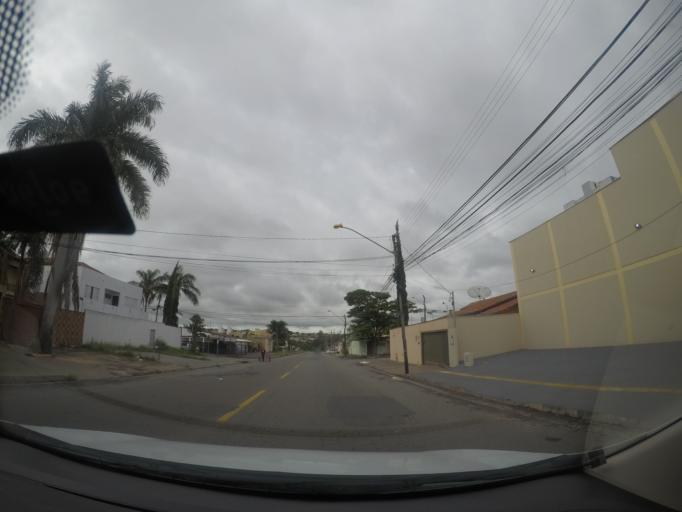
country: BR
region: Goias
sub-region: Goiania
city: Goiania
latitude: -16.7216
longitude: -49.2906
